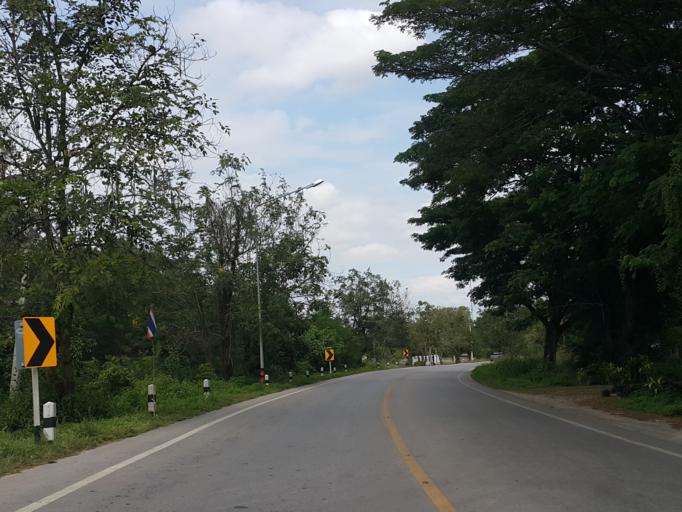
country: TH
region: Lampang
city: Lampang
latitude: 18.3365
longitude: 99.4594
